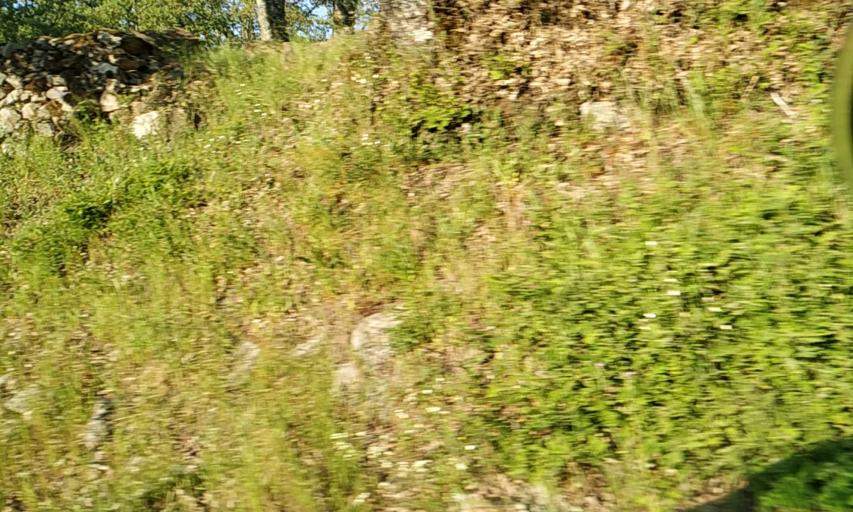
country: PT
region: Portalegre
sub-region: Marvao
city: Marvao
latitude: 39.3546
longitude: -7.4066
